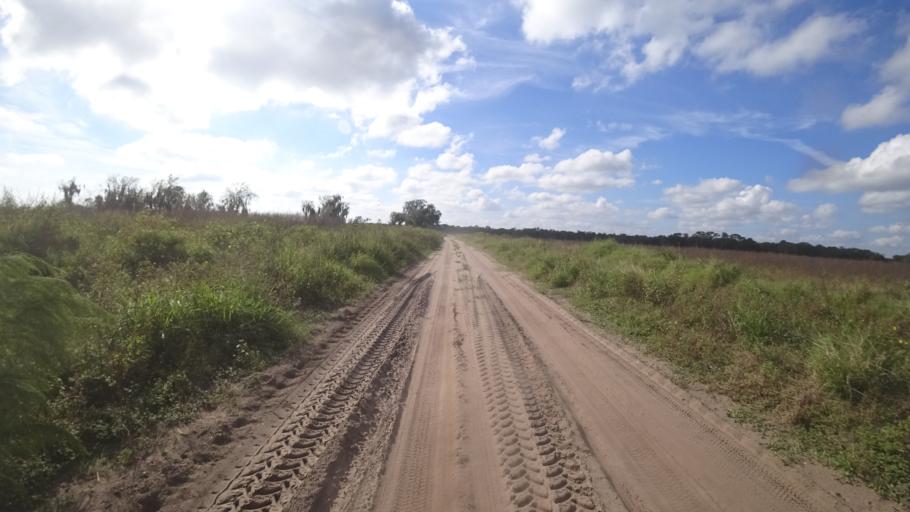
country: US
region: Florida
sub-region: DeSoto County
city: Arcadia
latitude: 27.3463
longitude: -82.1095
